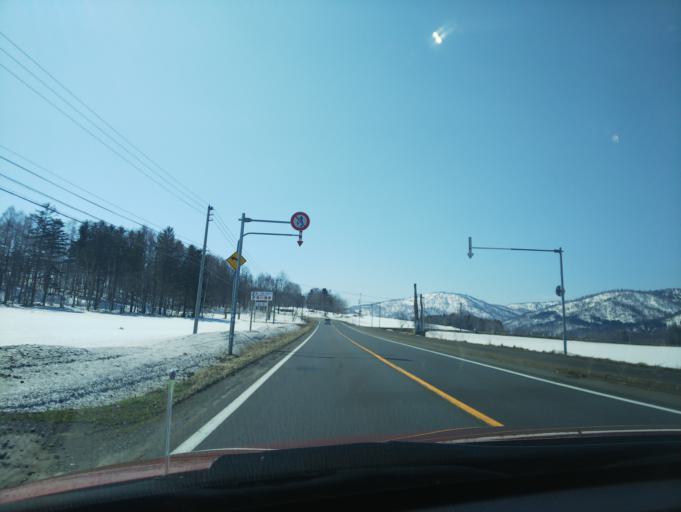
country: JP
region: Hokkaido
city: Nayoro
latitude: 44.6678
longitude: 142.2685
